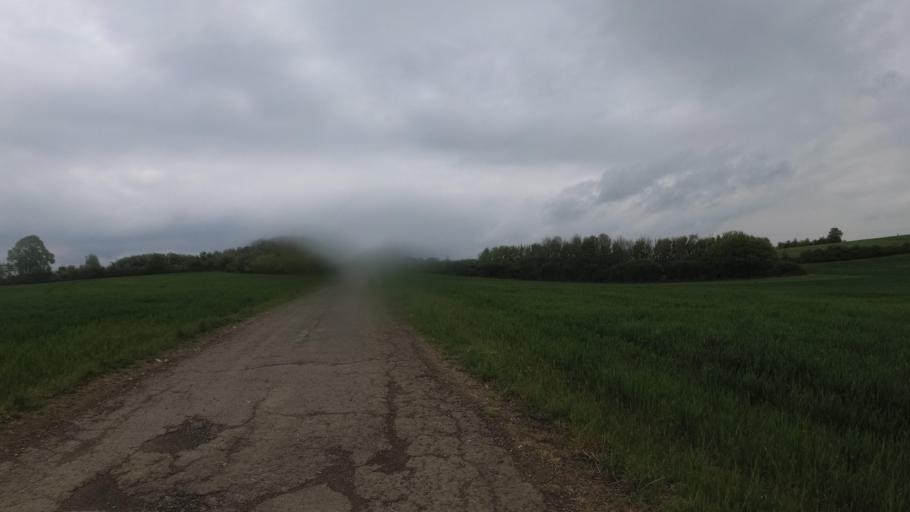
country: DE
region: Saarland
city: Rehlingen-Siersburg
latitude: 49.3255
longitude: 6.6462
